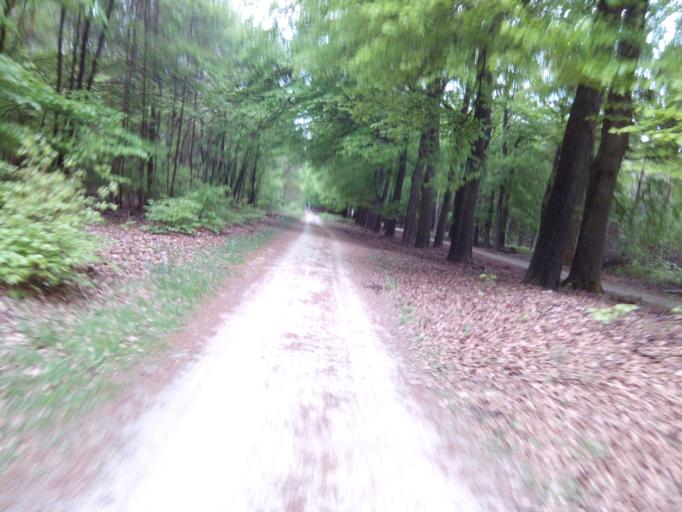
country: NL
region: Gelderland
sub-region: Gemeente Renkum
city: Wolfheze
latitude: 52.0359
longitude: 5.7843
